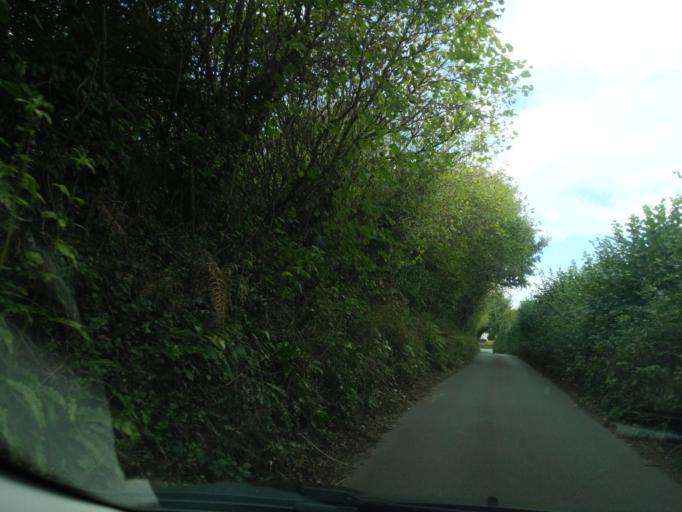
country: GB
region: England
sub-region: Plymouth
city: Plymstock
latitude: 50.3487
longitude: -4.0784
